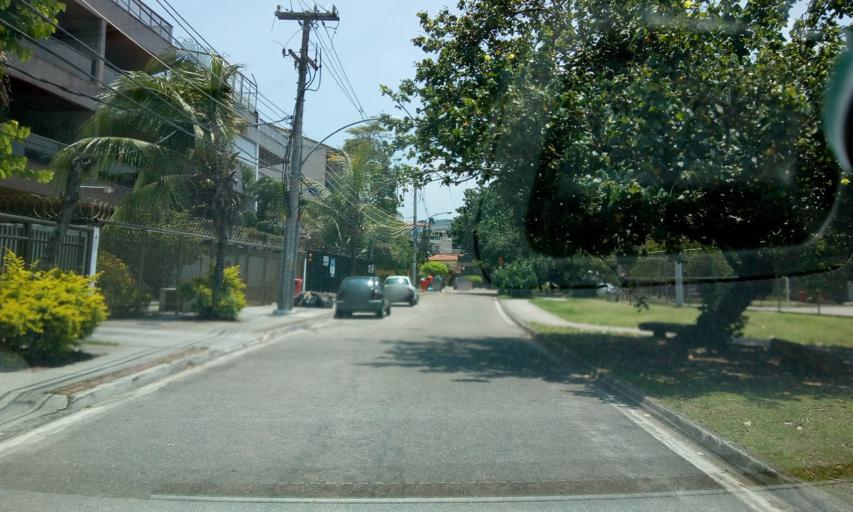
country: BR
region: Rio de Janeiro
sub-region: Nilopolis
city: Nilopolis
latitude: -23.0202
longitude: -43.4674
